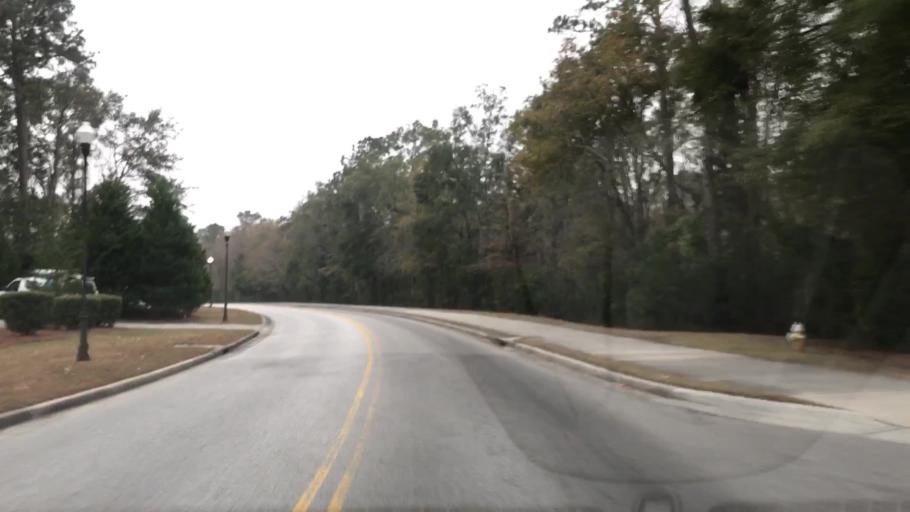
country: US
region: South Carolina
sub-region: Charleston County
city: Shell Point
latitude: 32.8052
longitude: -80.0798
